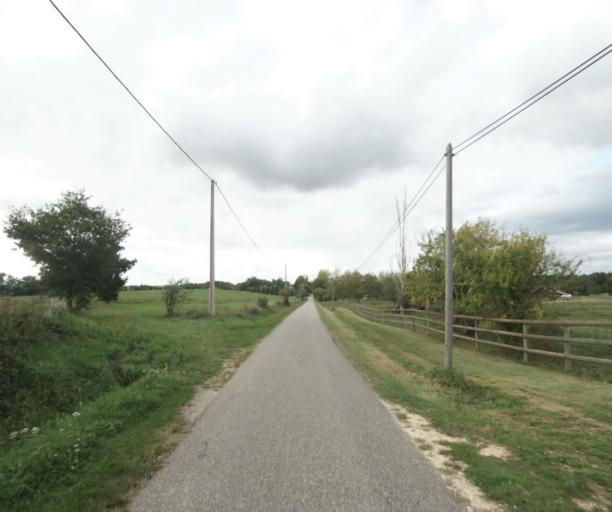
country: FR
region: Midi-Pyrenees
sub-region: Departement du Gers
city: Eauze
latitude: 43.9239
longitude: 0.0863
